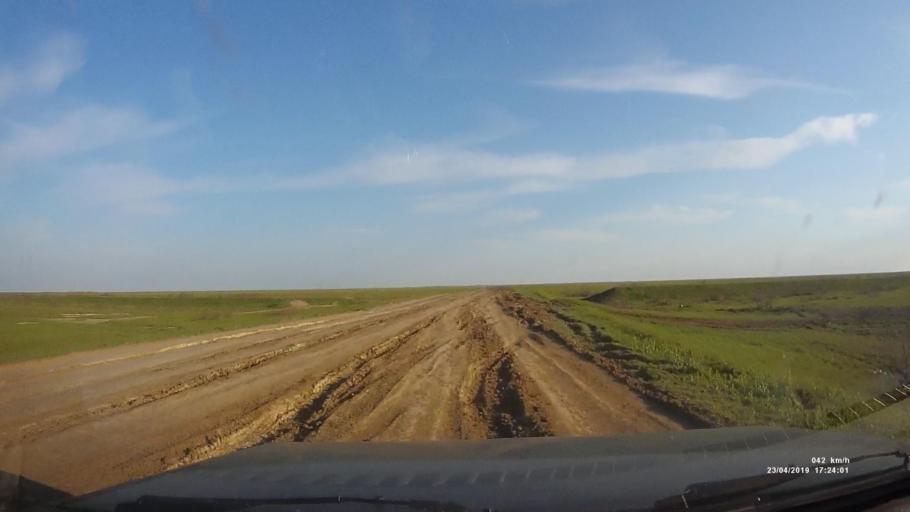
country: RU
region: Kalmykiya
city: Priyutnoye
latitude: 46.1589
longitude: 43.5082
